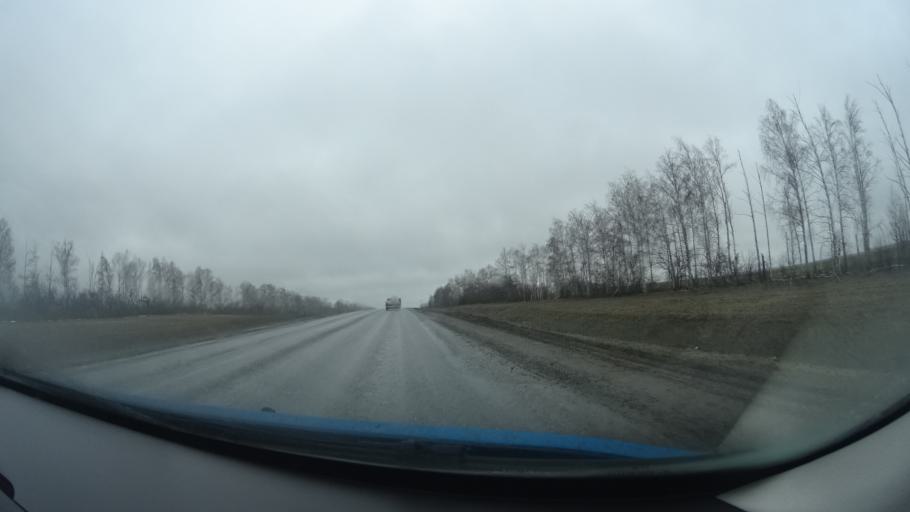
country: RU
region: Bashkortostan
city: Buzdyak
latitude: 54.6162
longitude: 54.3514
